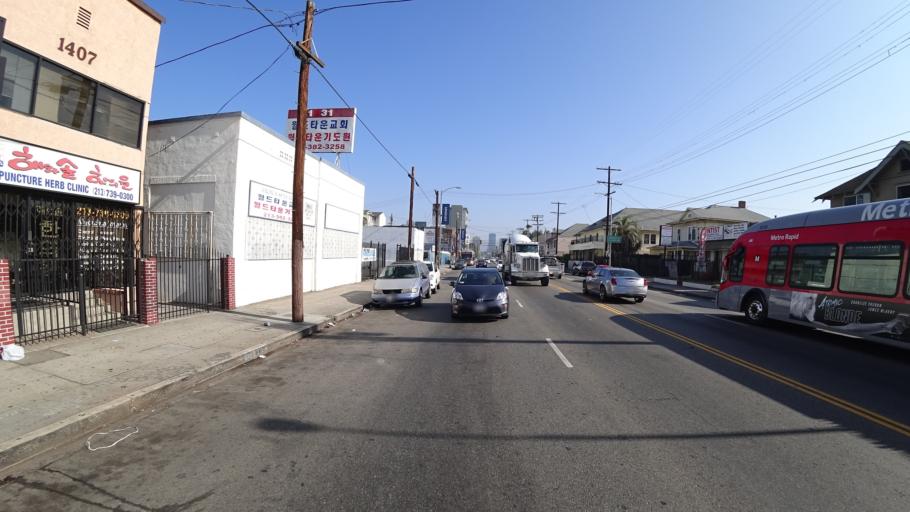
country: US
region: California
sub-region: Los Angeles County
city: Echo Park
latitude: 34.0461
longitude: -118.2917
